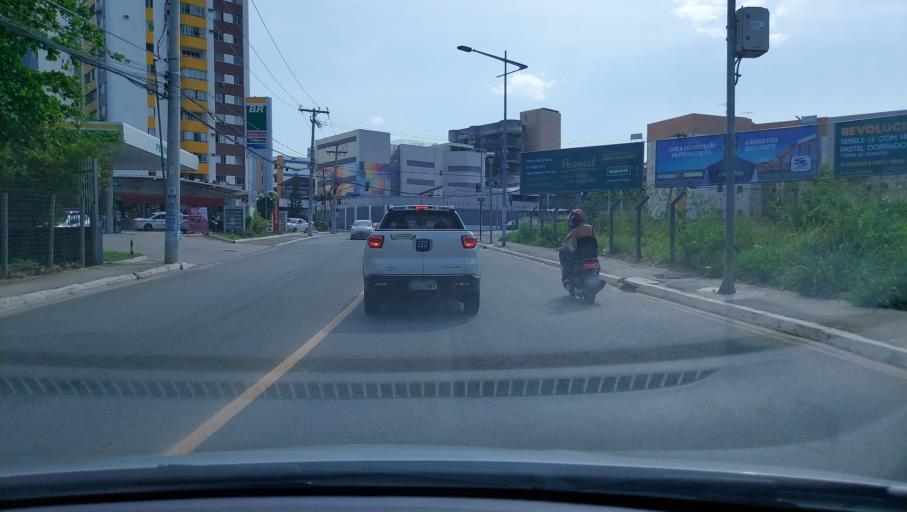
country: BR
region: Bahia
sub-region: Salvador
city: Salvador
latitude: -12.9813
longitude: -38.4426
